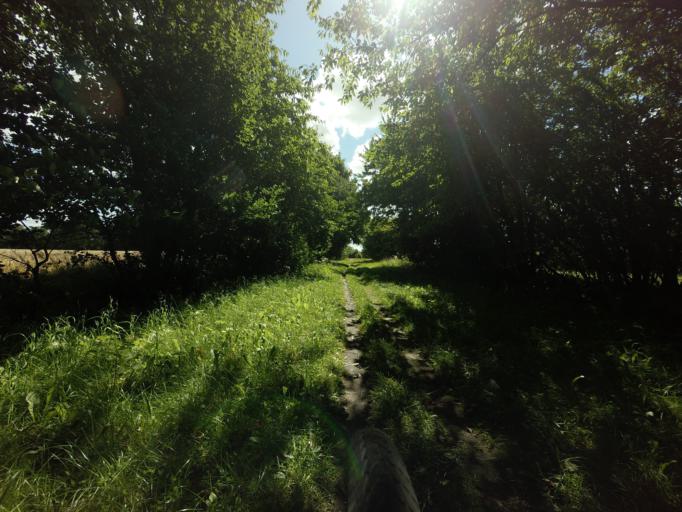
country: DK
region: Central Jutland
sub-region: Horsens Kommune
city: Horsens
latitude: 55.8885
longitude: 9.7827
